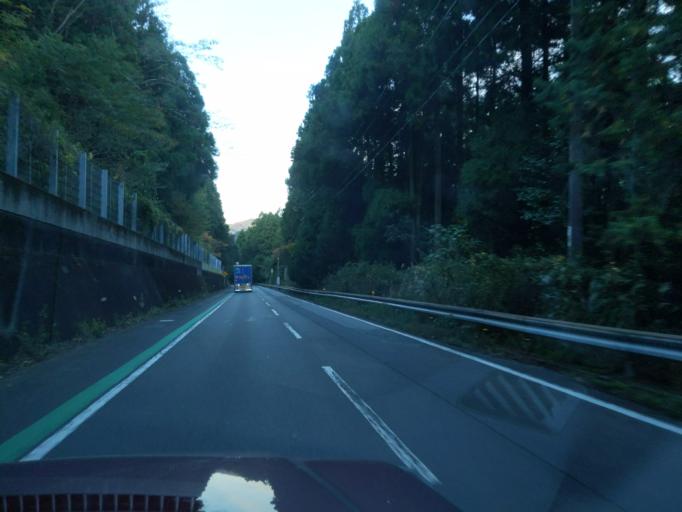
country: JP
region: Tokushima
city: Anan
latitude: 33.7068
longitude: 134.4558
